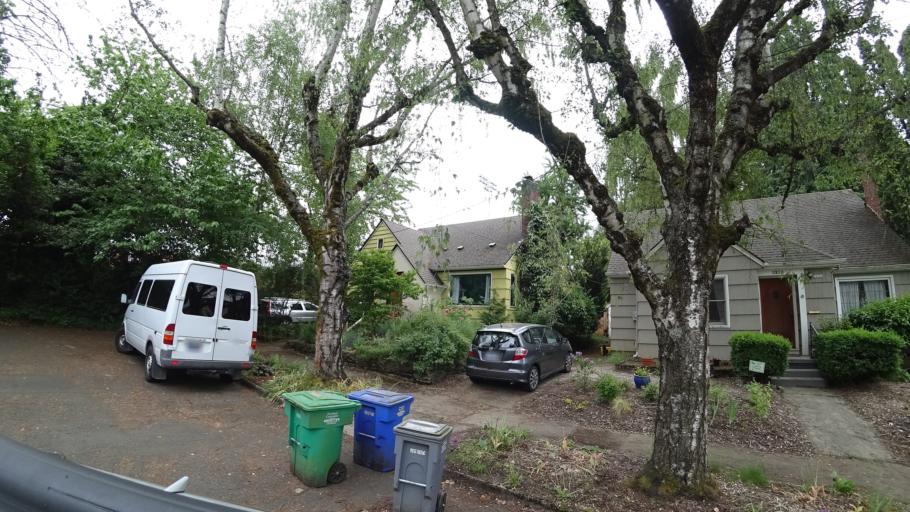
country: US
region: Oregon
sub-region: Multnomah County
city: Lents
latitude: 45.5042
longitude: -122.6081
